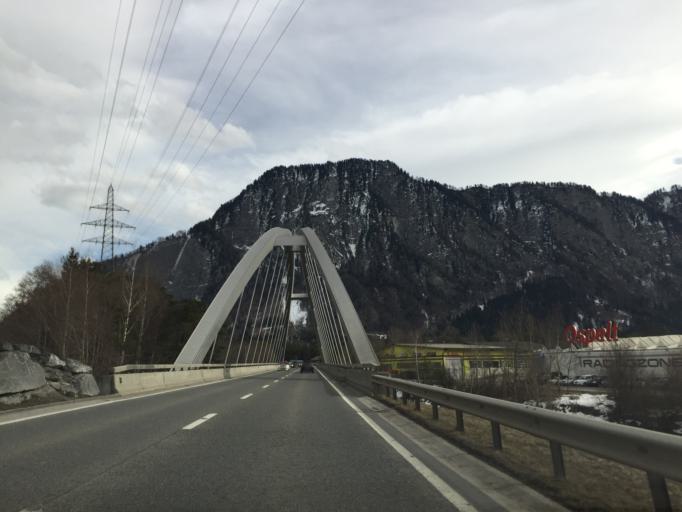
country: CH
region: Grisons
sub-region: Landquart District
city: Malans
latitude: 46.9699
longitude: 9.5740
